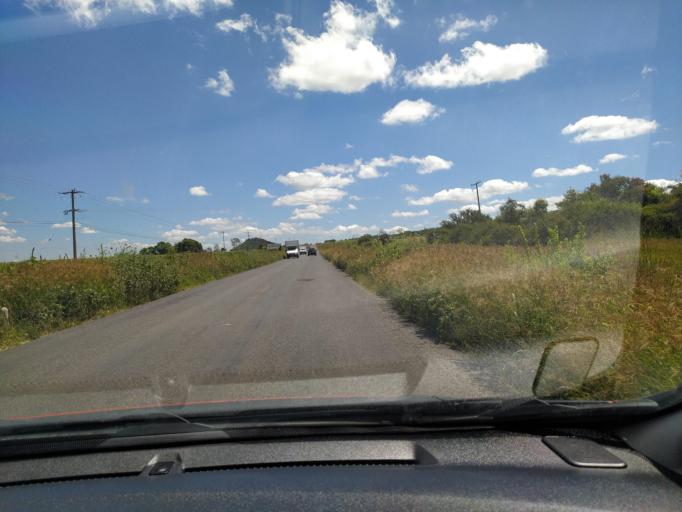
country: MX
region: Jalisco
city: San Julian
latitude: 21.0068
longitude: -102.1328
